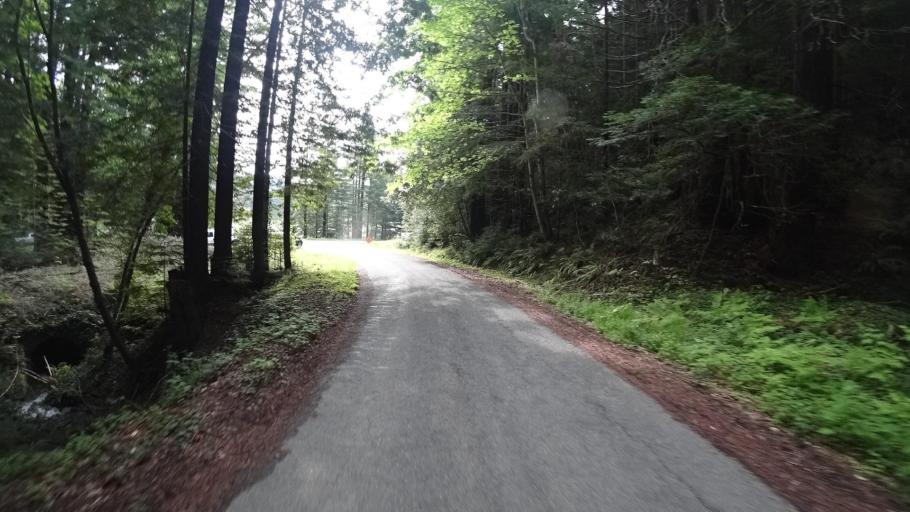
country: US
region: California
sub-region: Humboldt County
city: Redway
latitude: 40.3283
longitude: -123.8432
